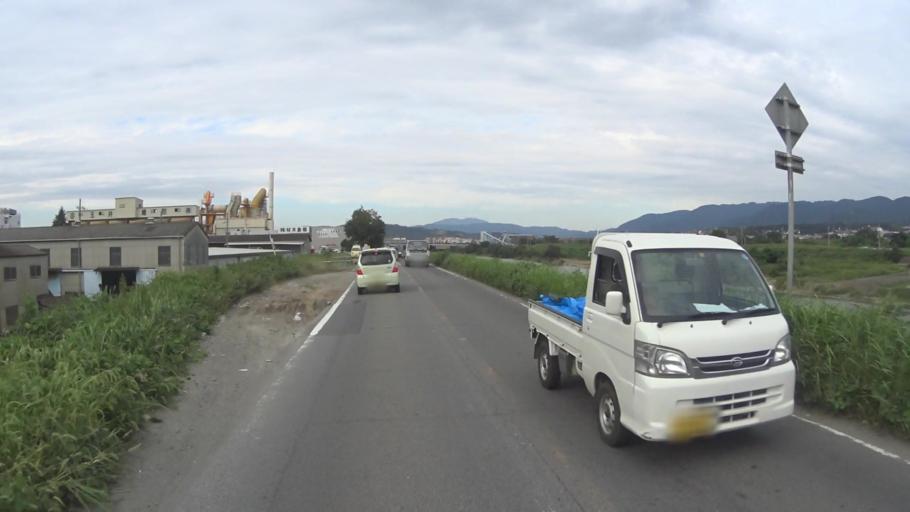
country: JP
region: Kyoto
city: Uji
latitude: 34.9100
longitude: 135.7891
